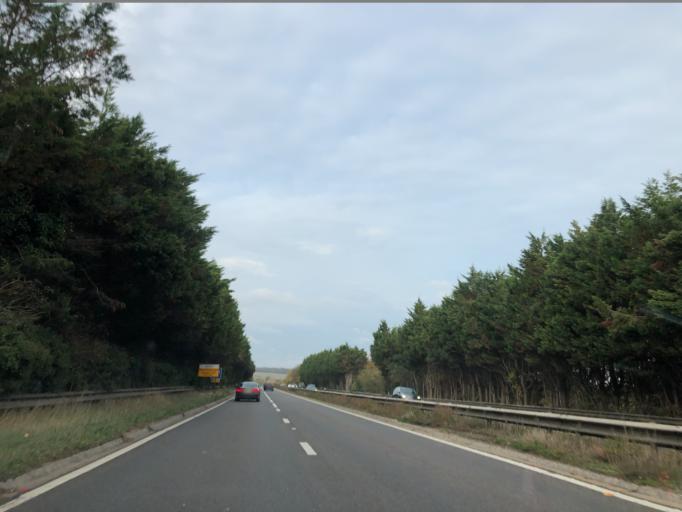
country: GB
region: England
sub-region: Buckinghamshire
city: Marlow
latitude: 51.5675
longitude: -0.7612
